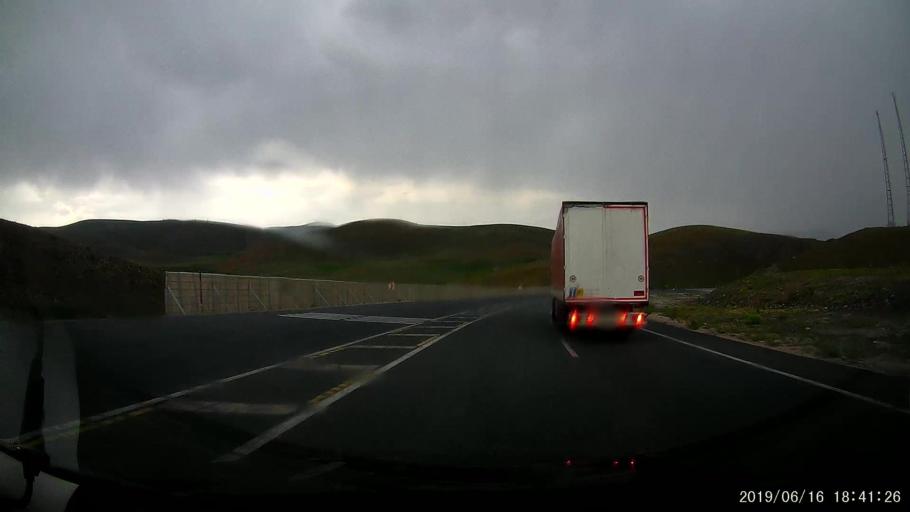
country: TR
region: Erzincan
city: Catalarmut
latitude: 39.8730
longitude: 39.1287
